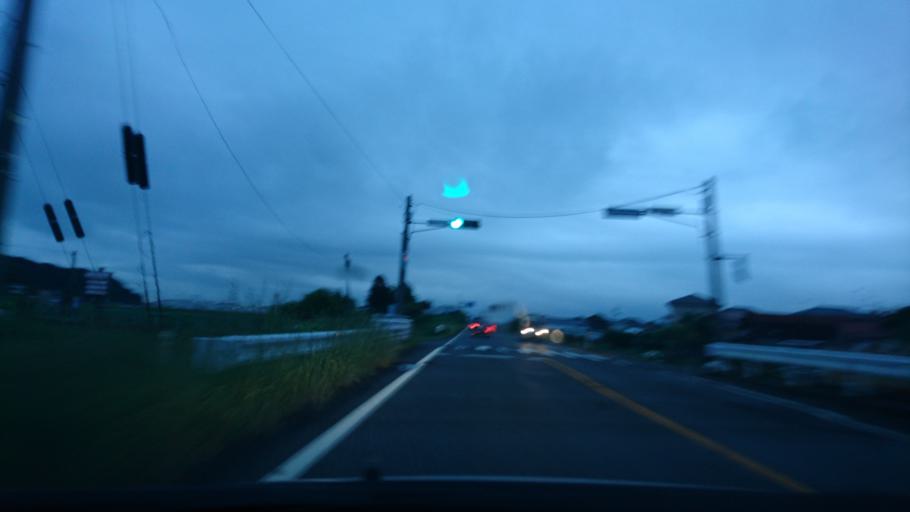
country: JP
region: Iwate
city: Ichinoseki
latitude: 38.8154
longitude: 141.0769
